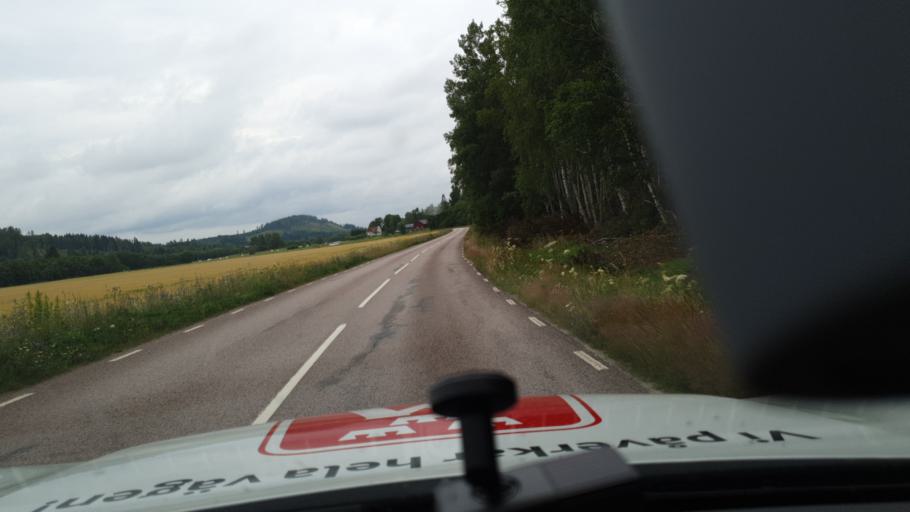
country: SE
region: Vaermland
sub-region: Sunne Kommun
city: Sunne
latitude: 59.7872
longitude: 13.2328
